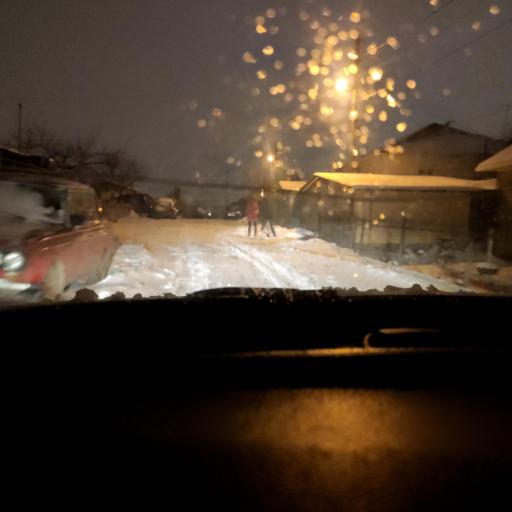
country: RU
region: Voronezj
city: Maslovka
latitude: 51.6114
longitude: 39.2246
